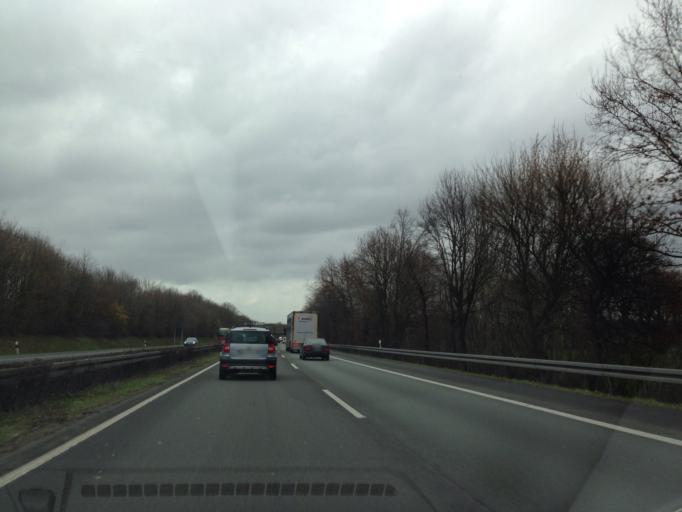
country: DE
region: North Rhine-Westphalia
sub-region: Regierungsbezirk Munster
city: Recklinghausen
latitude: 51.6321
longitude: 7.1675
